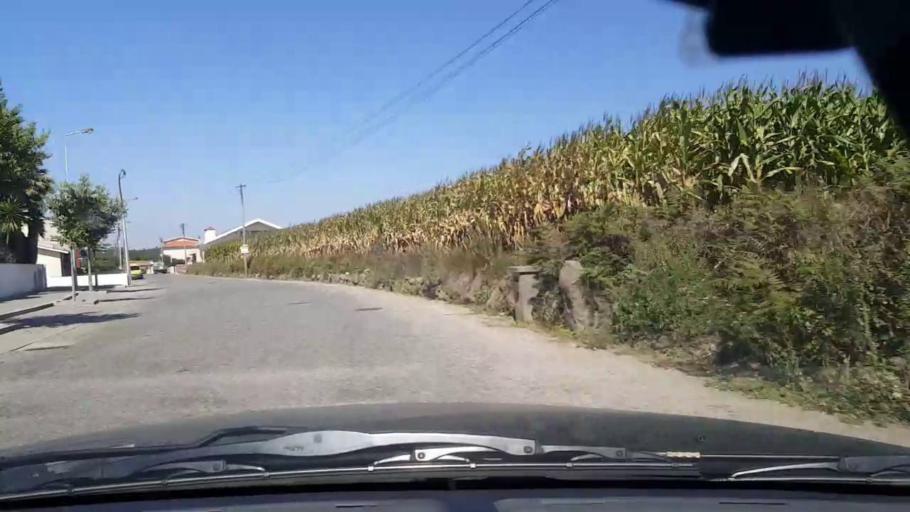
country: PT
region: Porto
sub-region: Matosinhos
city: Lavra
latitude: 41.2903
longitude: -8.7259
